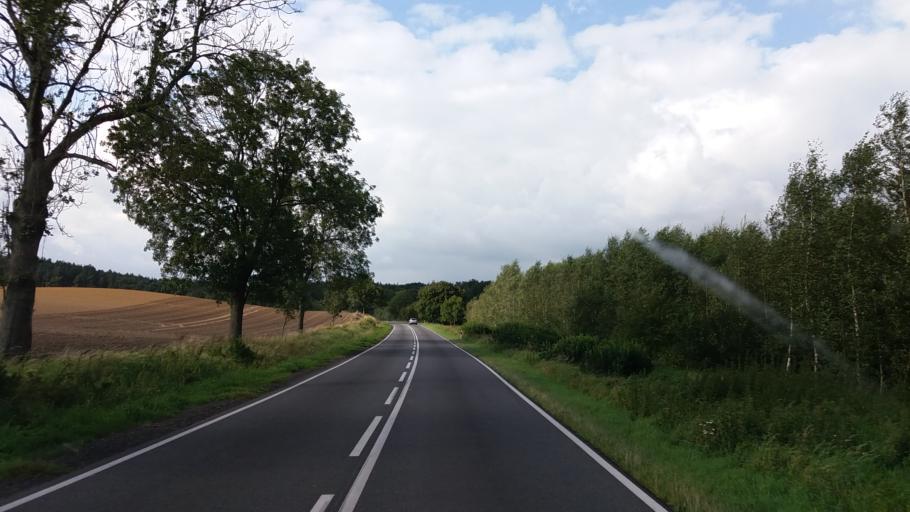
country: PL
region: West Pomeranian Voivodeship
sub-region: Powiat choszczenski
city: Pelczyce
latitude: 53.0605
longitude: 15.3019
